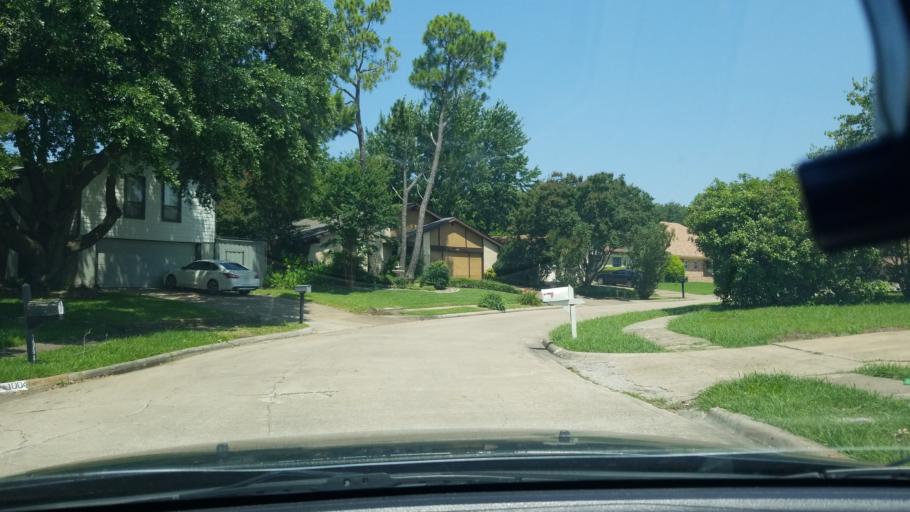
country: US
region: Texas
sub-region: Dallas County
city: Sunnyvale
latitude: 32.8289
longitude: -96.6107
